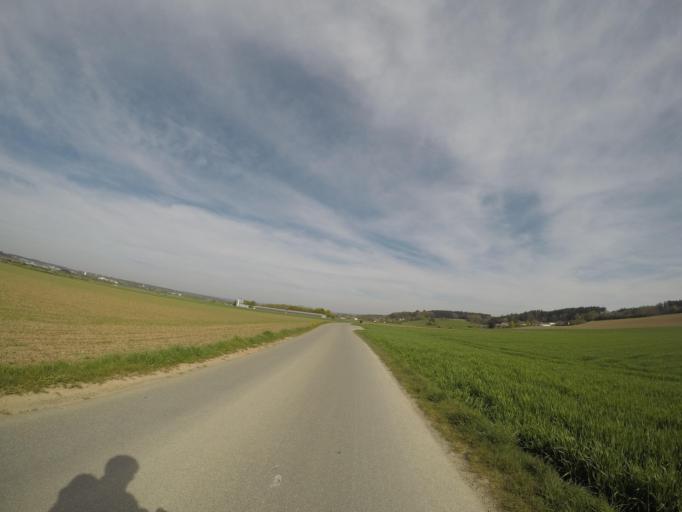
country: DE
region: Baden-Wuerttemberg
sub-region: Tuebingen Region
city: Saulgau
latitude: 48.0096
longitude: 9.5412
